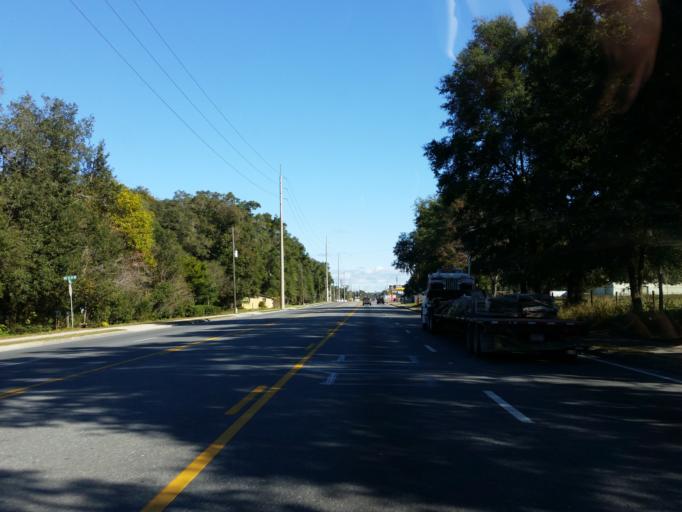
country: US
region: Florida
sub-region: Marion County
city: Ocala
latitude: 29.2669
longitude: -82.1867
